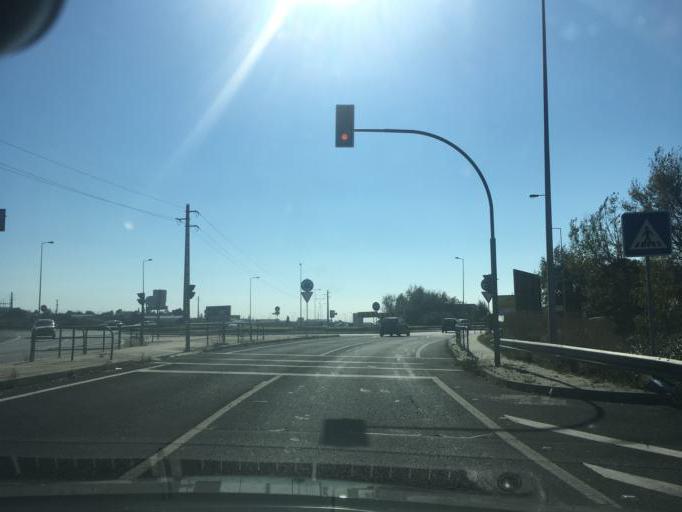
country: PT
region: Lisbon
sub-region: Oeiras
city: Barcarena
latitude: 38.7366
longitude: -9.2986
